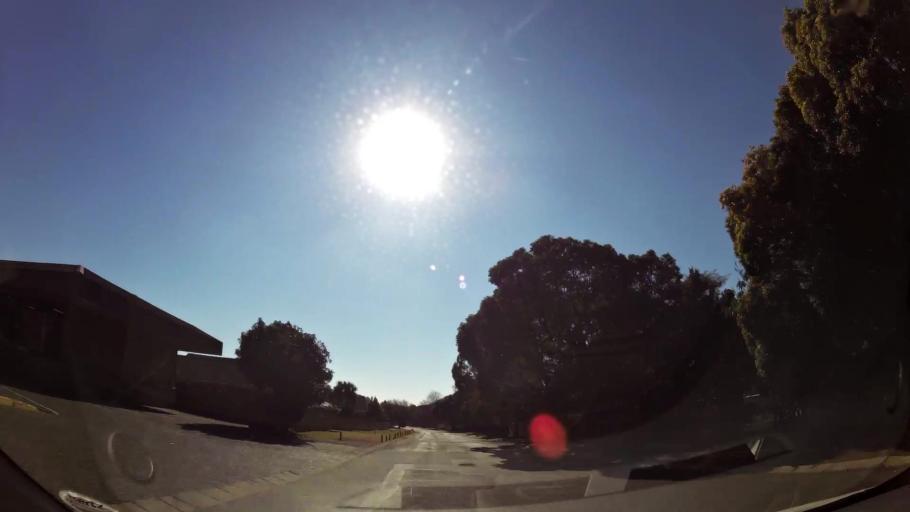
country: ZA
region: Mpumalanga
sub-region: Nkangala District Municipality
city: Witbank
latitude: -25.8878
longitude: 29.2350
